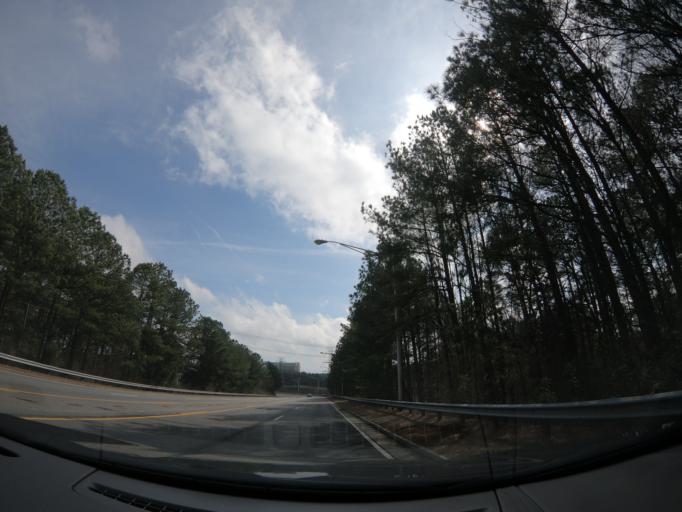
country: US
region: Georgia
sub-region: Fulton County
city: College Park
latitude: 33.6317
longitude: -84.4647
